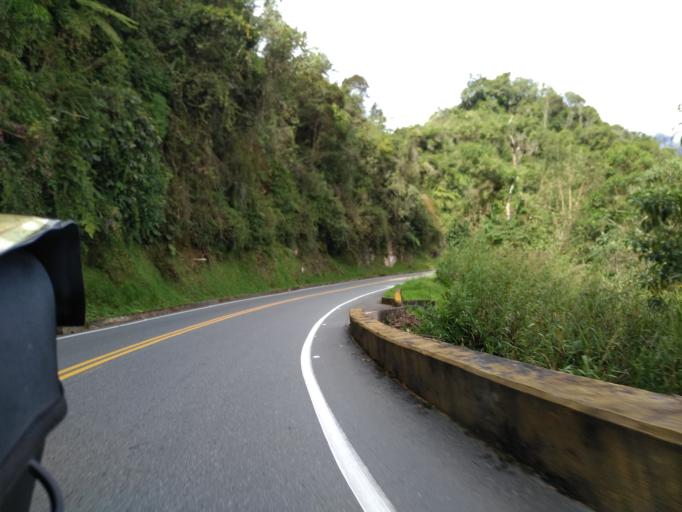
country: CO
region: Tolima
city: Herveo
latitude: 5.1005
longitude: -75.2293
